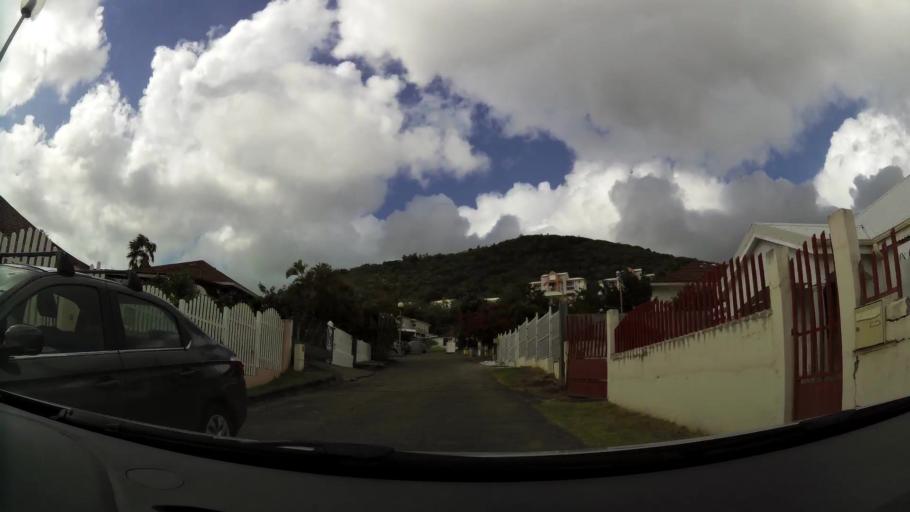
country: MQ
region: Martinique
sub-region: Martinique
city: Sainte-Luce
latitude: 14.4676
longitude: -60.9305
